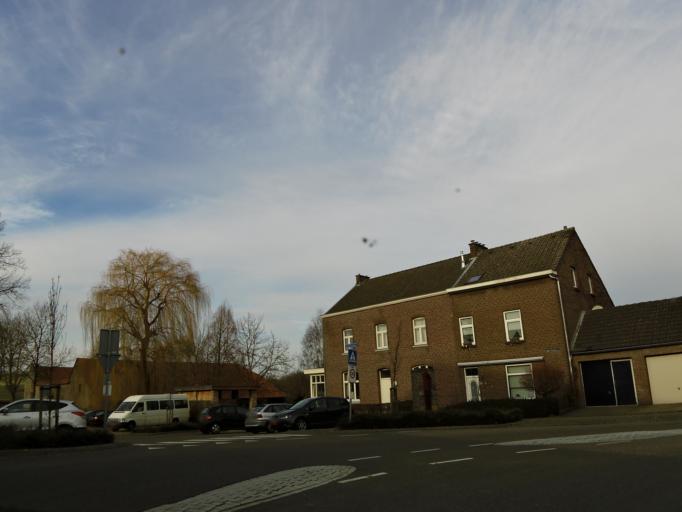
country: NL
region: Limburg
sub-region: Gemeente Voerendaal
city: Ubachsberg
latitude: 50.8091
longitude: 5.9185
